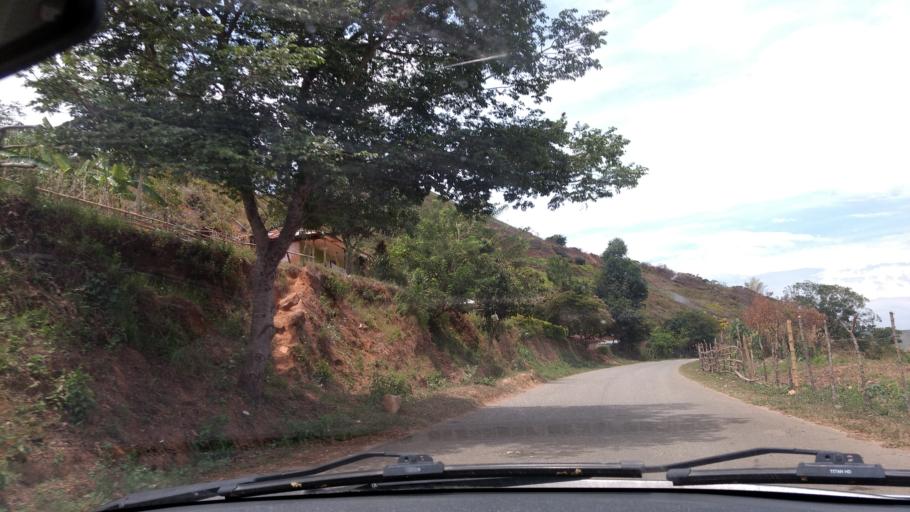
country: CO
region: Cauca
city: Buenos Aires
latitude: 3.0418
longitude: -76.6696
